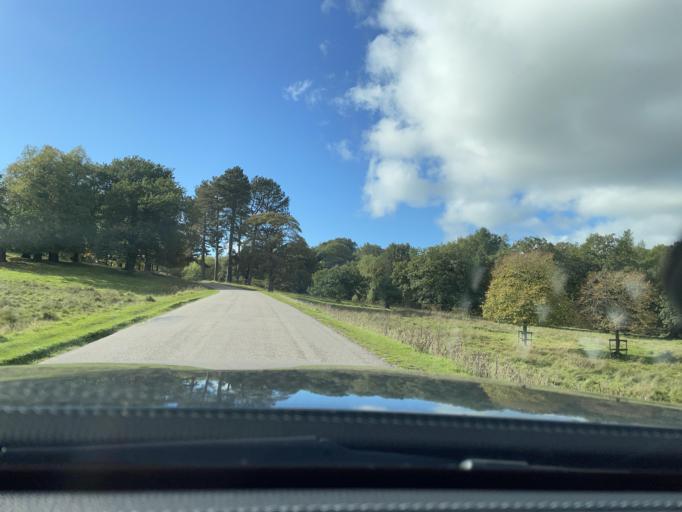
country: GB
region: England
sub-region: Cheshire East
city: Disley
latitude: 53.3533
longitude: -2.0531
